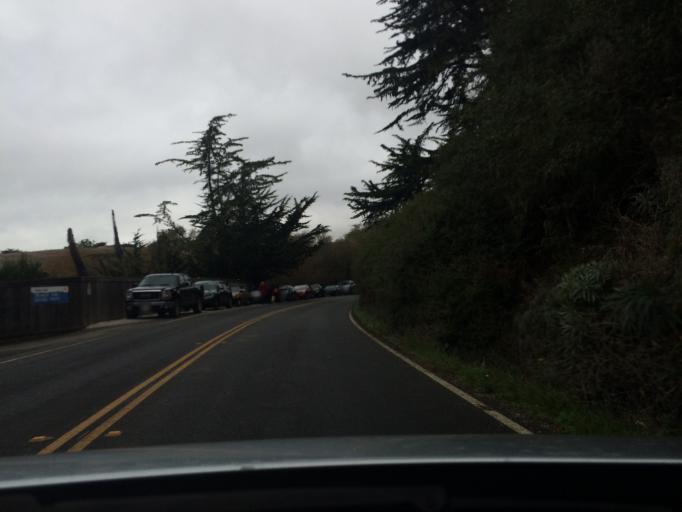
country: US
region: California
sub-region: Marin County
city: Inverness
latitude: 38.1621
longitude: -122.8934
